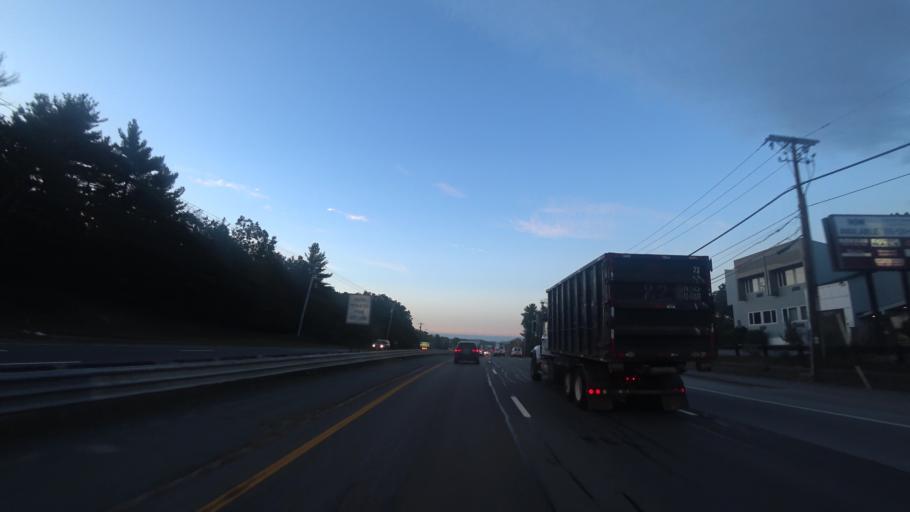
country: US
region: Massachusetts
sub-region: Essex County
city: Saugus
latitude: 42.5024
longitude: -71.0147
